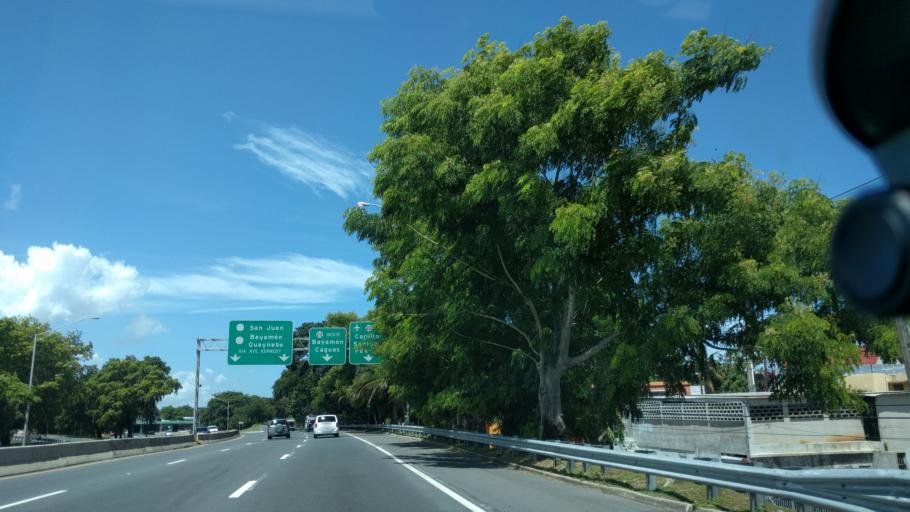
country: PR
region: San Juan
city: San Juan
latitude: 18.4402
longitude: -66.0661
